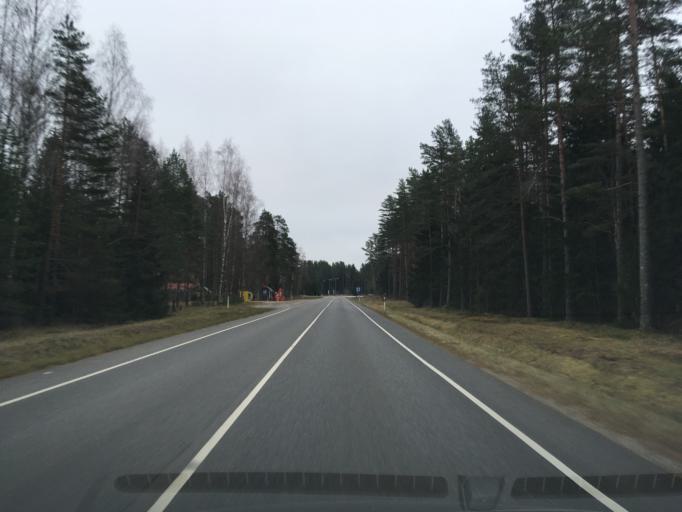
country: EE
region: Laeaene-Virumaa
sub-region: Kadrina vald
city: Kadrina
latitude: 59.4535
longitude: 26.0248
